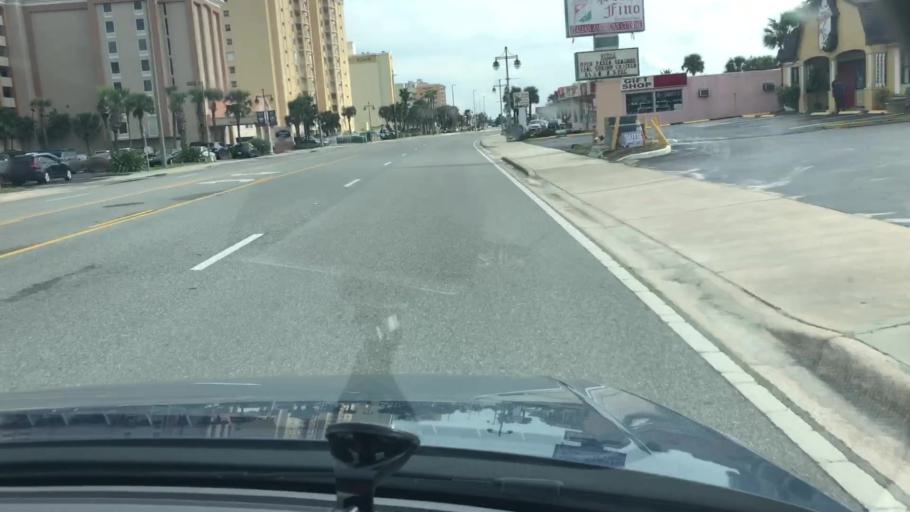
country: US
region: Florida
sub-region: Volusia County
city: Daytona Beach Shores
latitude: 29.1636
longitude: -80.9758
